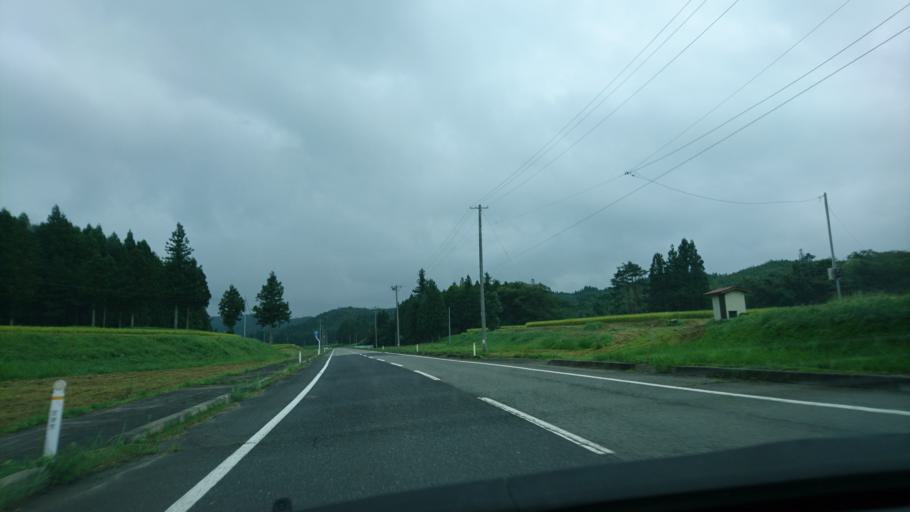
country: JP
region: Iwate
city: Ichinoseki
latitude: 38.8871
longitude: 140.9613
